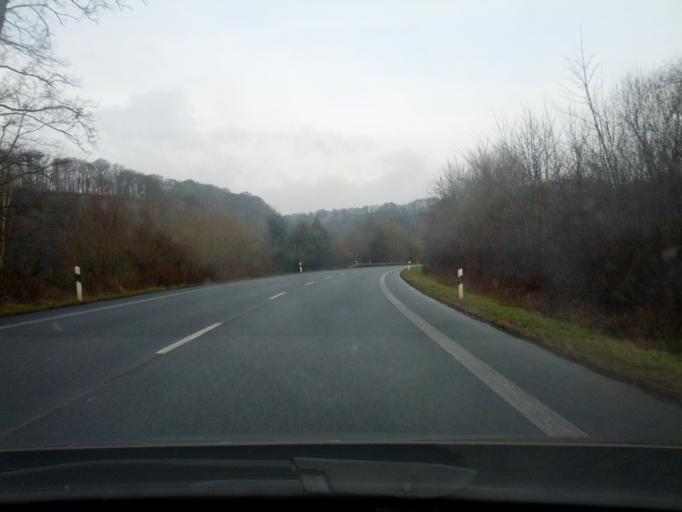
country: DE
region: Lower Saxony
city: Scheden
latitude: 51.3950
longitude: 9.7282
